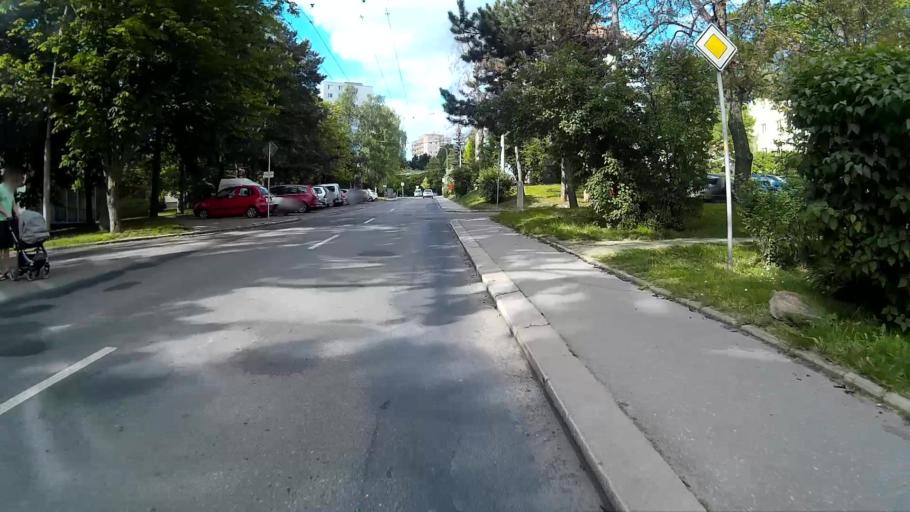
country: CZ
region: South Moravian
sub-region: Mesto Brno
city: Brno
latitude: 49.2140
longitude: 16.5831
